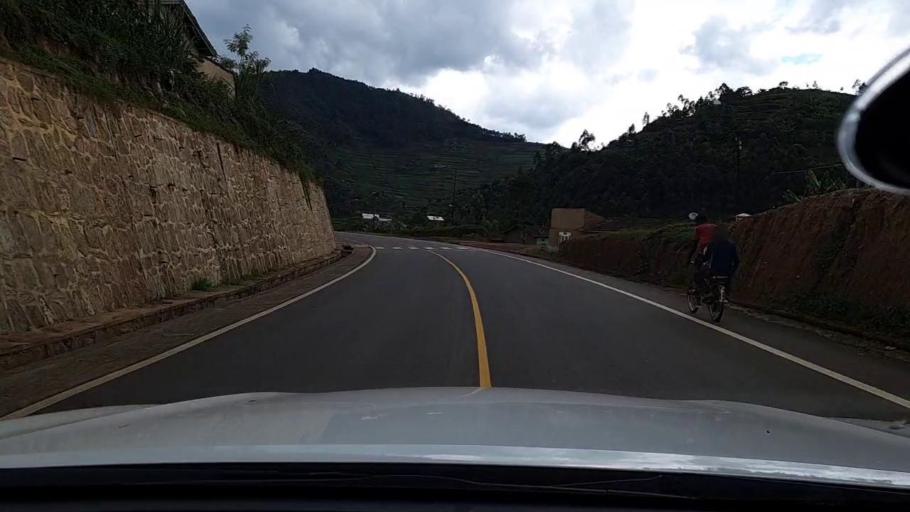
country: RW
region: Northern Province
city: Byumba
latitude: -1.6475
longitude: 29.9214
